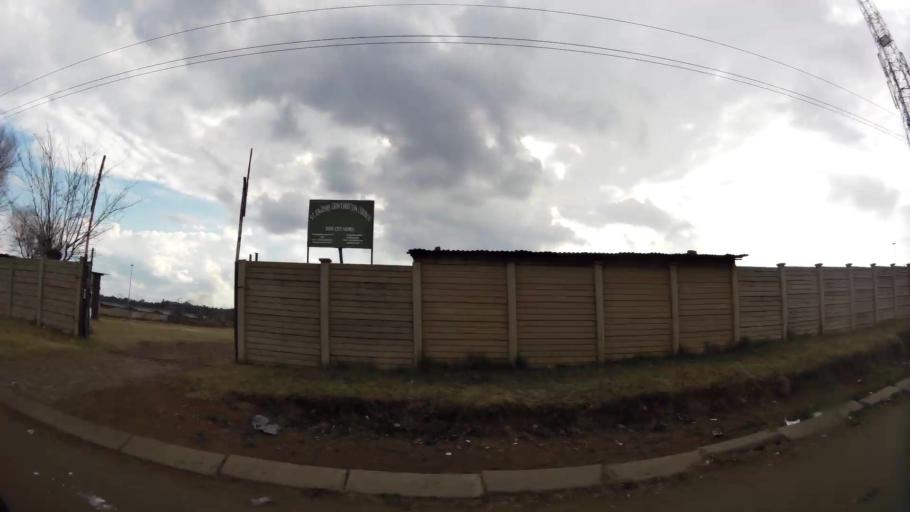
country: ZA
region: Gauteng
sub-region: Sedibeng District Municipality
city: Vanderbijlpark
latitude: -26.6645
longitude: 27.8463
